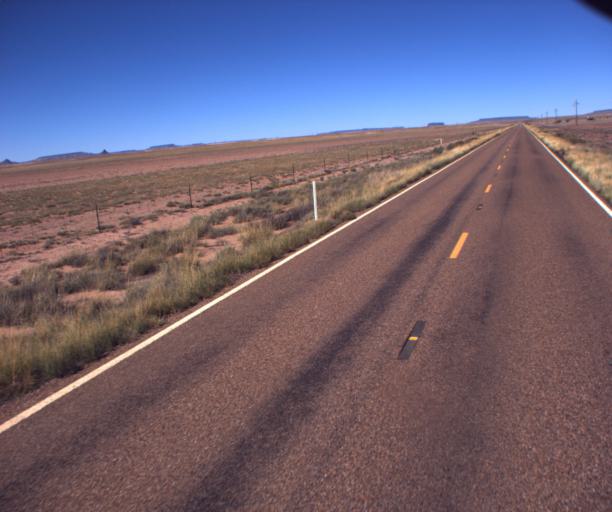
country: US
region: Arizona
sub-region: Navajo County
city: Holbrook
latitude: 35.0931
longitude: -110.0969
